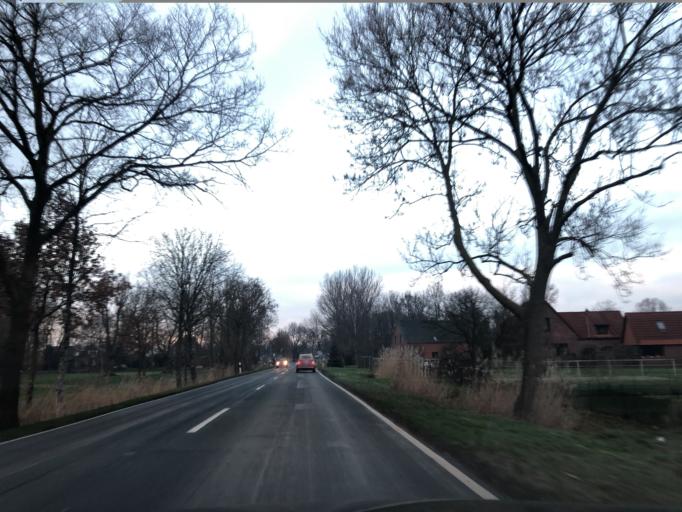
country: DE
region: Lower Saxony
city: Lemwerder
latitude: 53.1274
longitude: 8.6282
